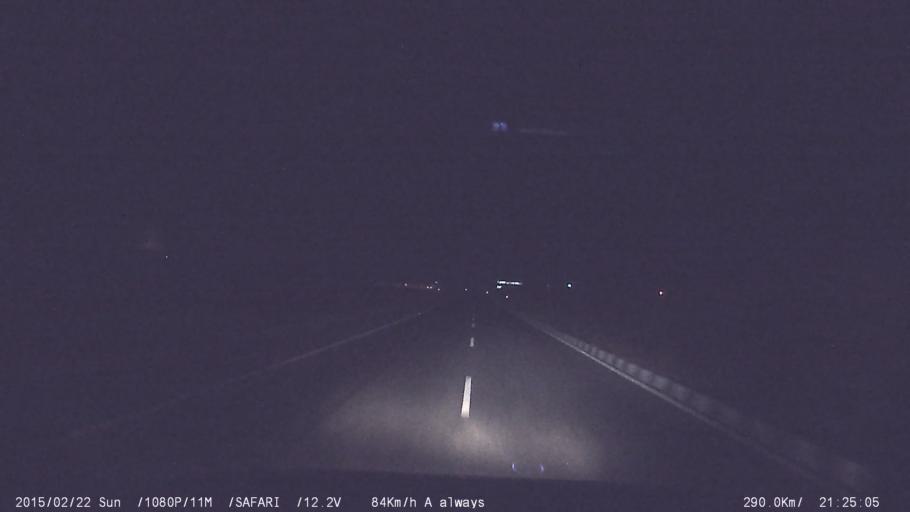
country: IN
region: Tamil Nadu
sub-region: Karur
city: Karur
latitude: 10.8931
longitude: 78.0246
